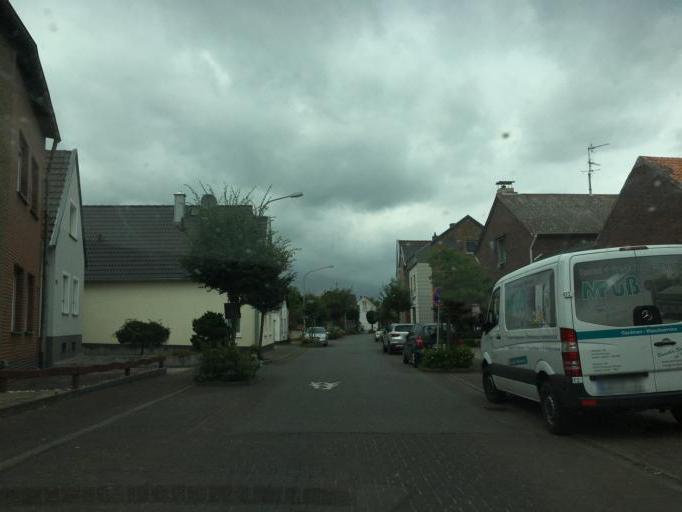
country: DE
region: North Rhine-Westphalia
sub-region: Regierungsbezirk Koln
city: Merzenich
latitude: 50.8130
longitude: 6.5536
